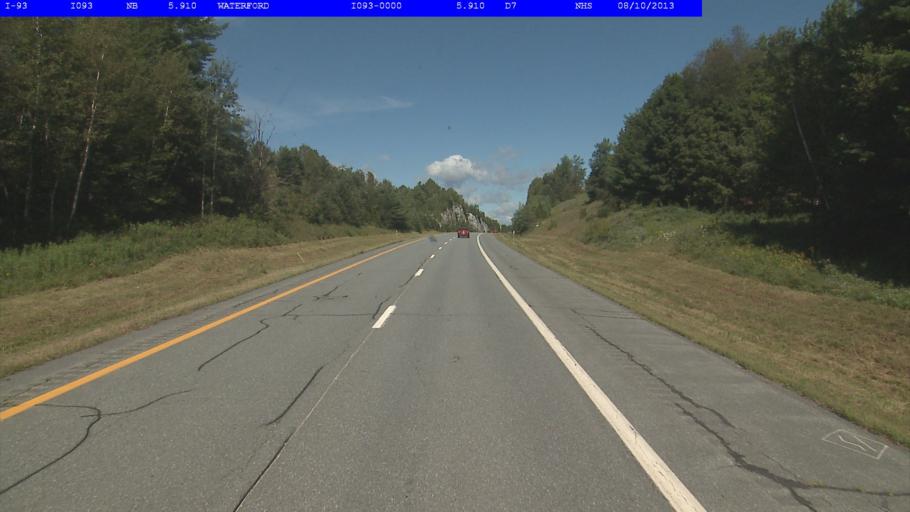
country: US
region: Vermont
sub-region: Caledonia County
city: Saint Johnsbury
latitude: 44.4180
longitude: -71.9290
